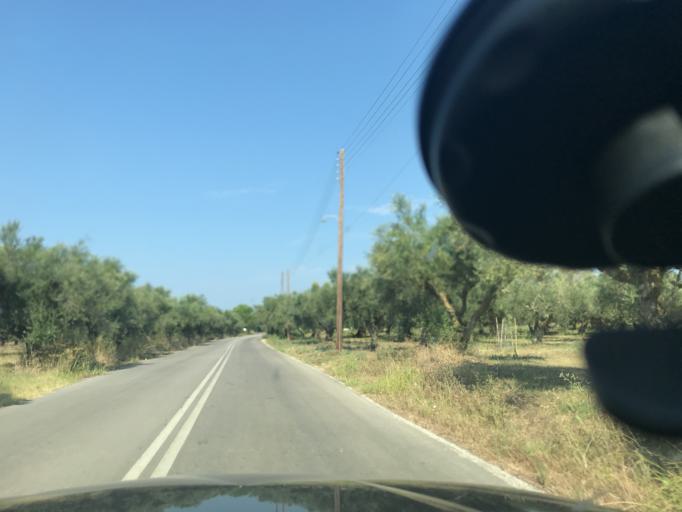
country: GR
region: West Greece
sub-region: Nomos Ileias
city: Kardamas
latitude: 37.7159
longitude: 21.3400
